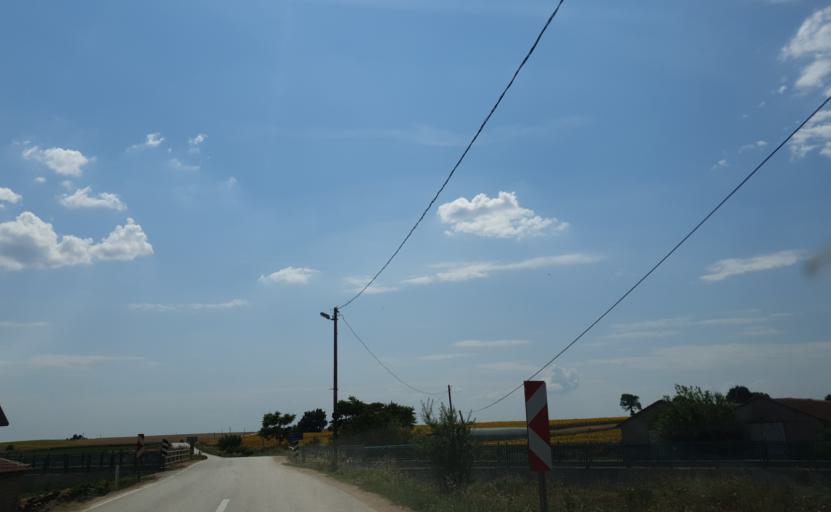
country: TR
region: Tekirdag
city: Beyazkoy
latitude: 41.4552
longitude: 27.6424
